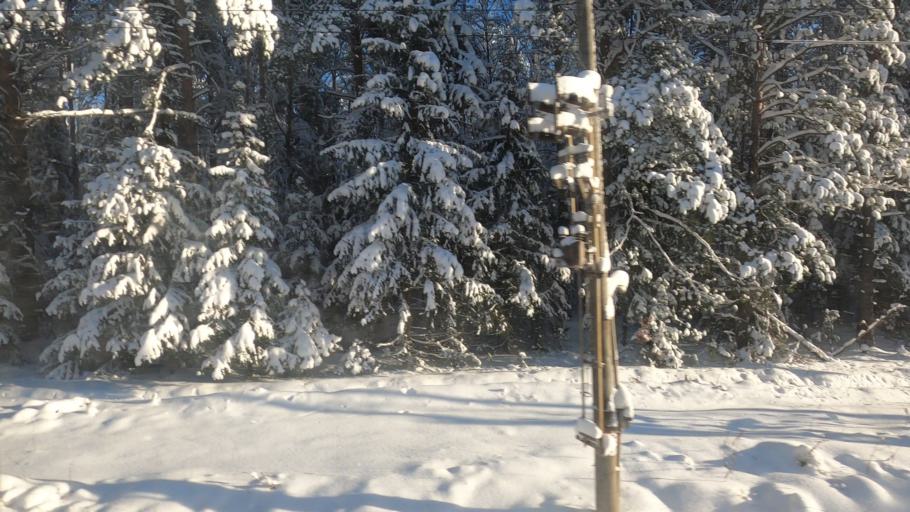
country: RU
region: Moskovskaya
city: Zhukovka
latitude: 56.4870
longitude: 37.5499
